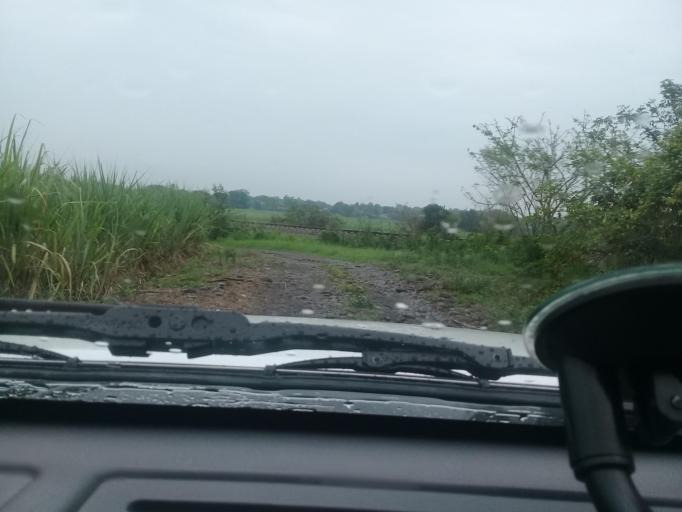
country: MX
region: Veracruz
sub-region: Puente Nacional
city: Cabezas
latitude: 19.3583
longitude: -96.3763
